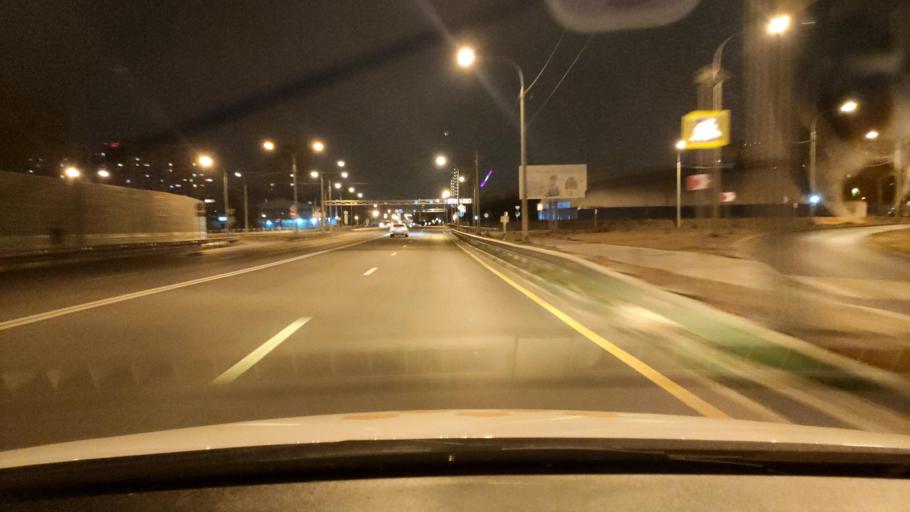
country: RU
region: Voronezj
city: Pridonskoy
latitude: 51.6849
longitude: 39.1158
